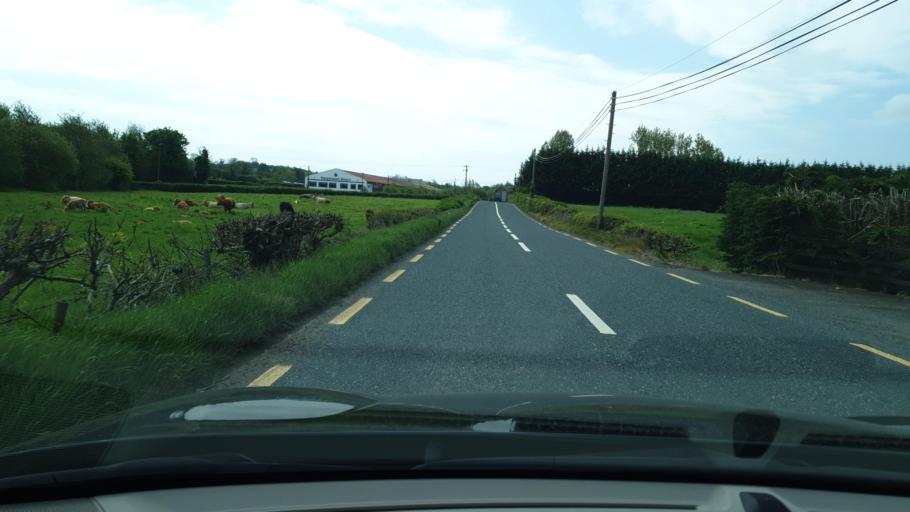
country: IE
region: Ulster
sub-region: An Cabhan
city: Kingscourt
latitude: 53.9092
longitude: -6.7878
